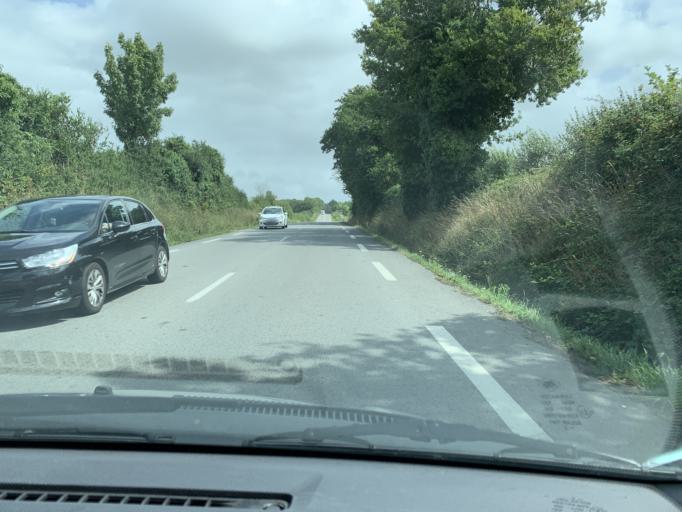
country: FR
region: Brittany
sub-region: Departement du Morbihan
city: Penestin
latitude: 47.4809
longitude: -2.4615
